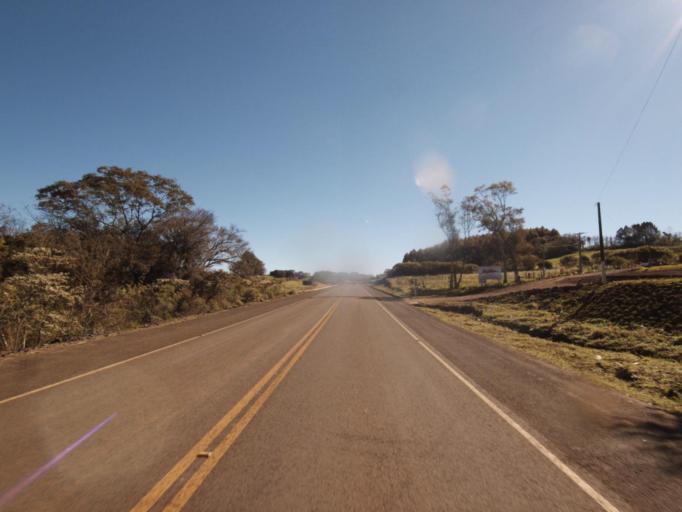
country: AR
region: Misiones
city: Bernardo de Irigoyen
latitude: -26.6136
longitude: -53.6769
